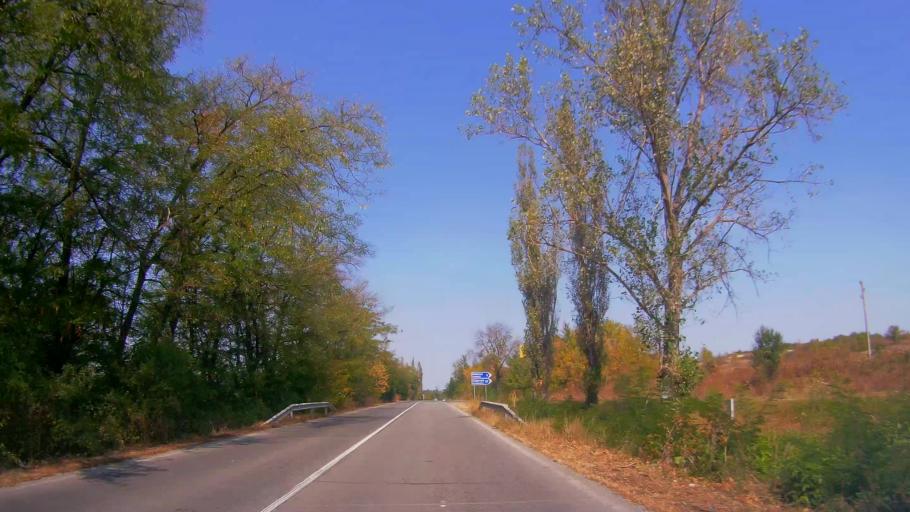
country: BG
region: Shumen
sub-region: Obshtina Smyadovo
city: Smyadovo
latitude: 43.1534
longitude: 27.0207
